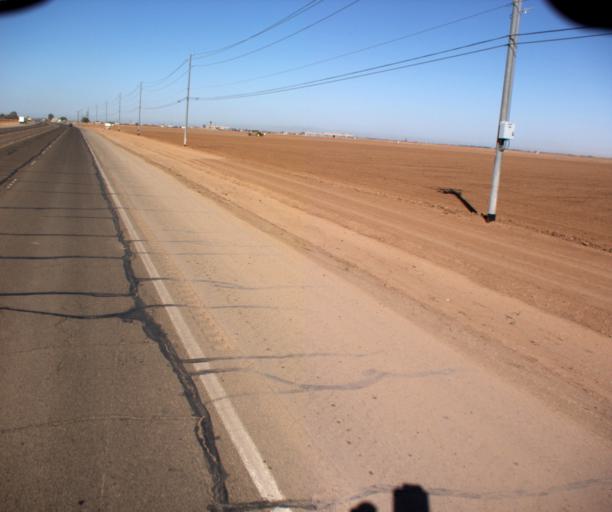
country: US
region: Arizona
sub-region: Yuma County
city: Somerton
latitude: 32.5967
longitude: -114.7541
